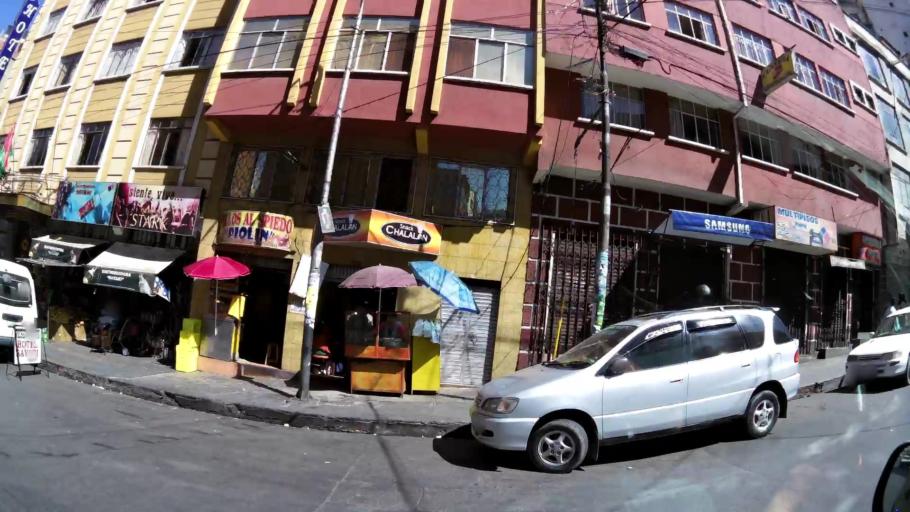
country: BO
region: La Paz
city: La Paz
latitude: -16.4937
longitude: -68.1420
